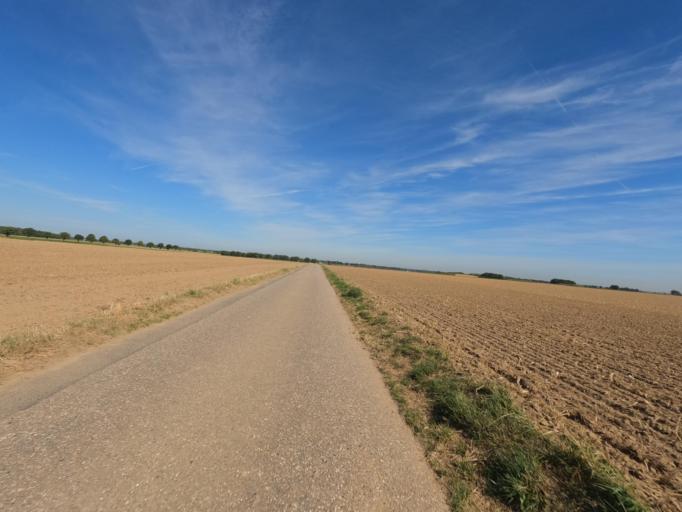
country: DE
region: North Rhine-Westphalia
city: Erkelenz
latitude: 51.0403
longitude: 6.3544
